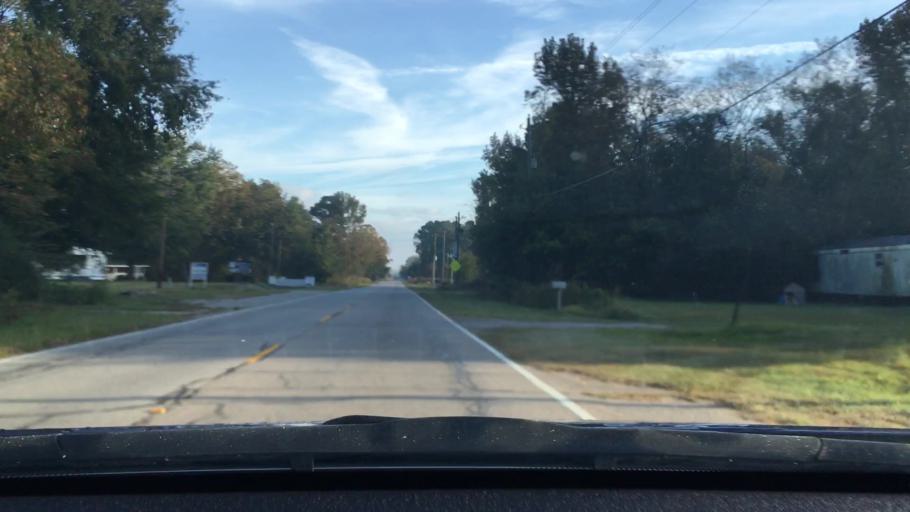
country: US
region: South Carolina
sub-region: Sumter County
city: East Sumter
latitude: 33.9432
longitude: -80.3153
